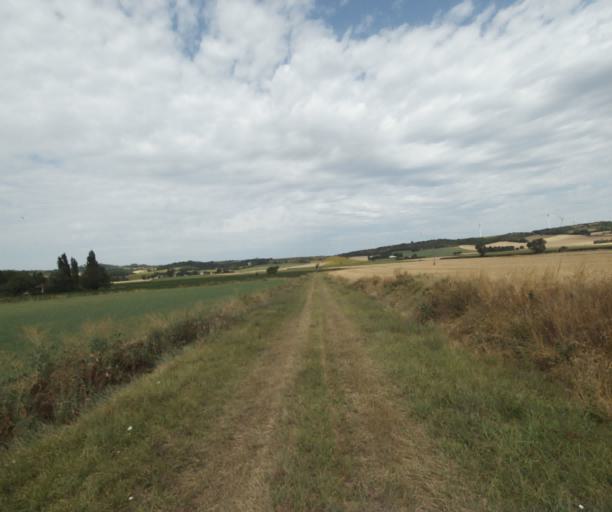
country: FR
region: Midi-Pyrenees
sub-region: Departement de la Haute-Garonne
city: Saint-Felix-Lauragais
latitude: 43.4488
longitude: 1.9292
